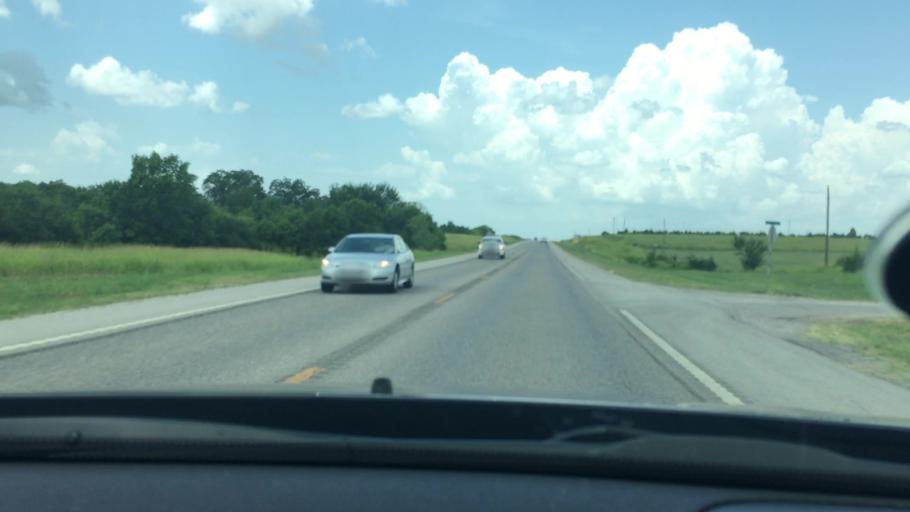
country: US
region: Oklahoma
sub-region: Marshall County
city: Oakland
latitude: 34.0999
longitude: -96.8498
